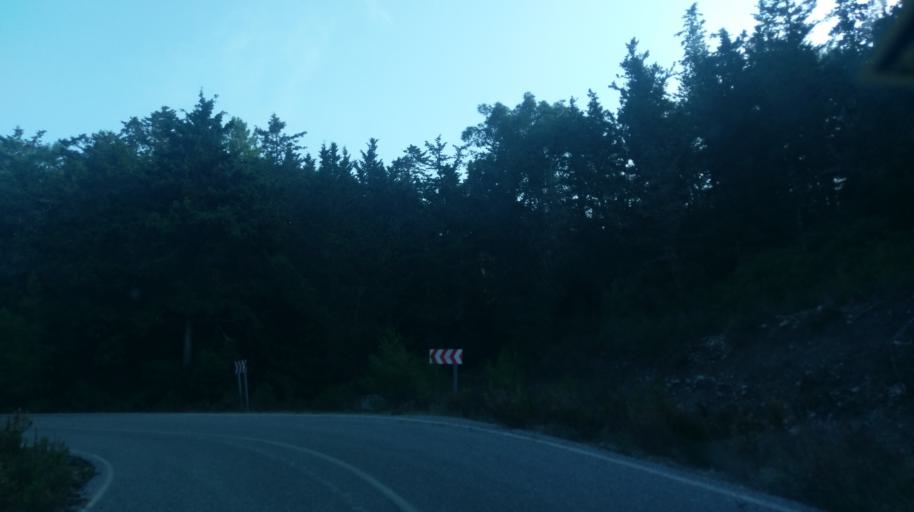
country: CY
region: Ammochostos
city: Trikomo
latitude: 35.3880
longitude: 33.8956
